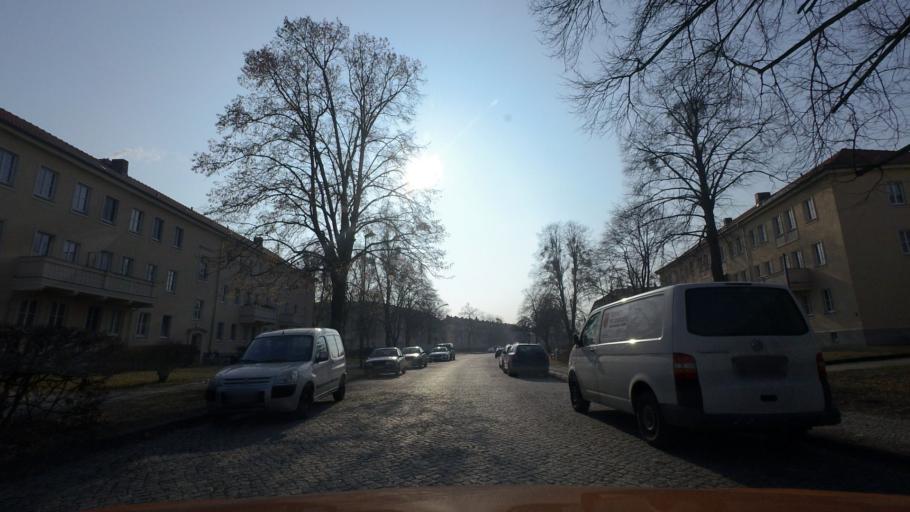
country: DE
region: Brandenburg
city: Ludwigsfelde
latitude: 52.3007
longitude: 13.2662
